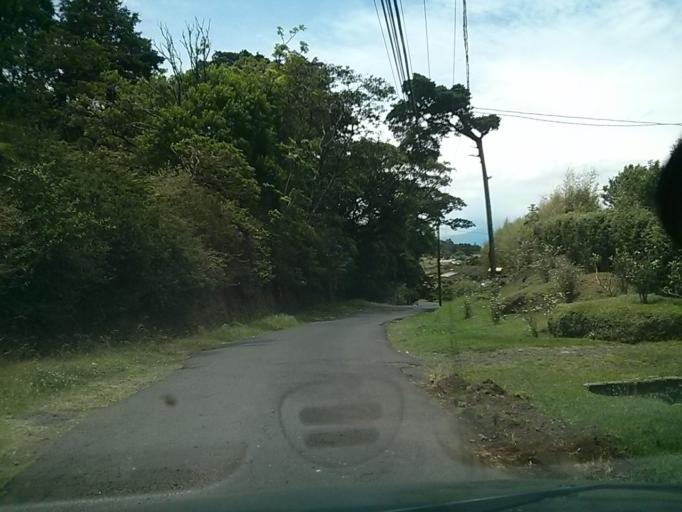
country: CR
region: Heredia
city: Santo Domingo
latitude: 10.0726
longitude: -84.1065
